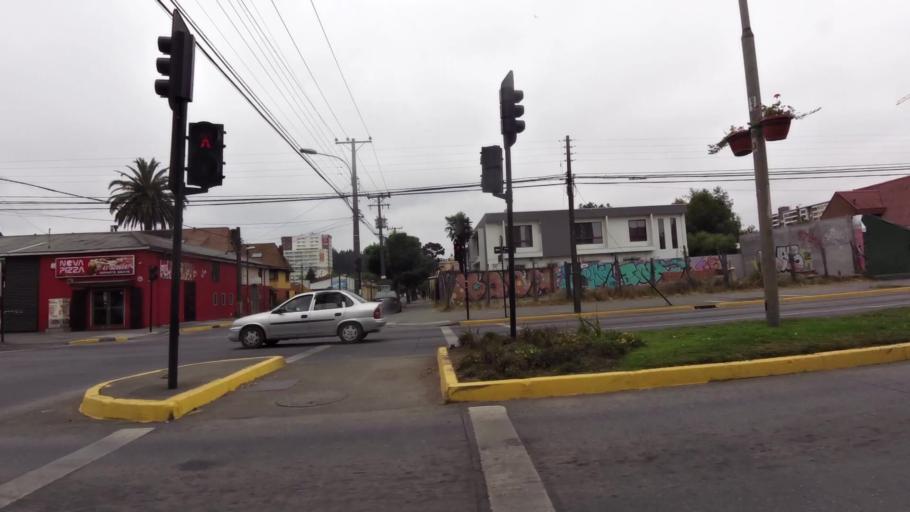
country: CL
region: Biobio
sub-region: Provincia de Concepcion
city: Concepcion
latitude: -36.8175
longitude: -73.0380
